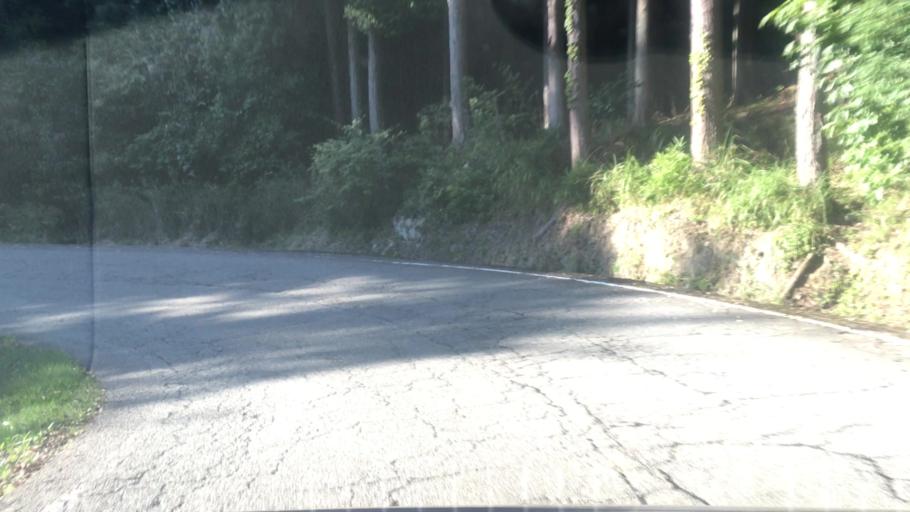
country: JP
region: Hyogo
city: Toyooka
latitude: 35.6205
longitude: 134.8715
